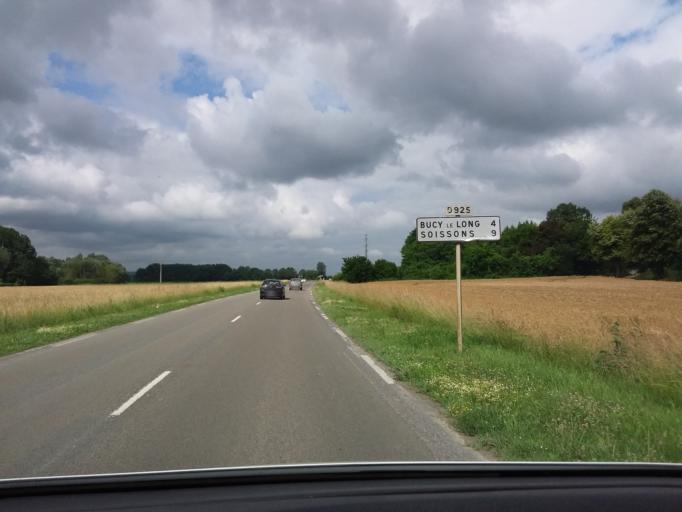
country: FR
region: Picardie
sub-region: Departement de l'Aisne
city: Bucy-le-Long
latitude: 49.3836
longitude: 3.4372
